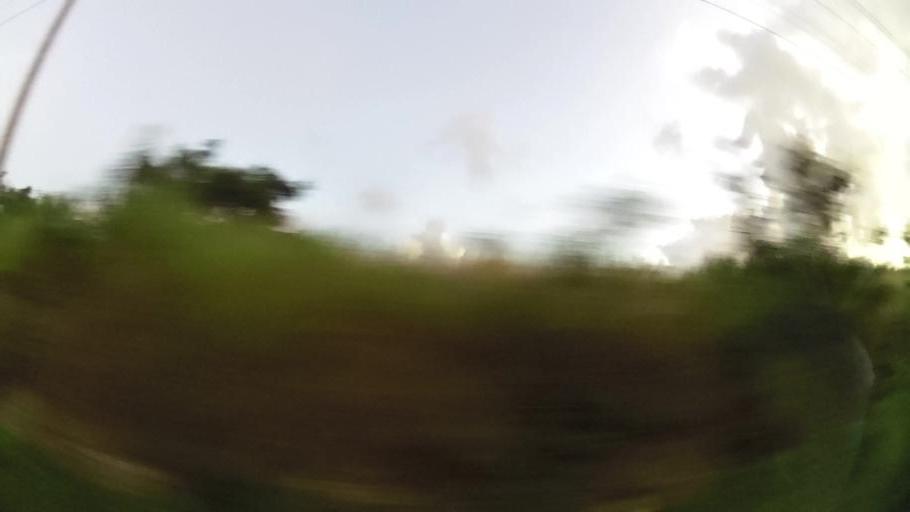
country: BB
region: Saint John
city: Four Cross Roads
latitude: 13.1193
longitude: -59.5203
